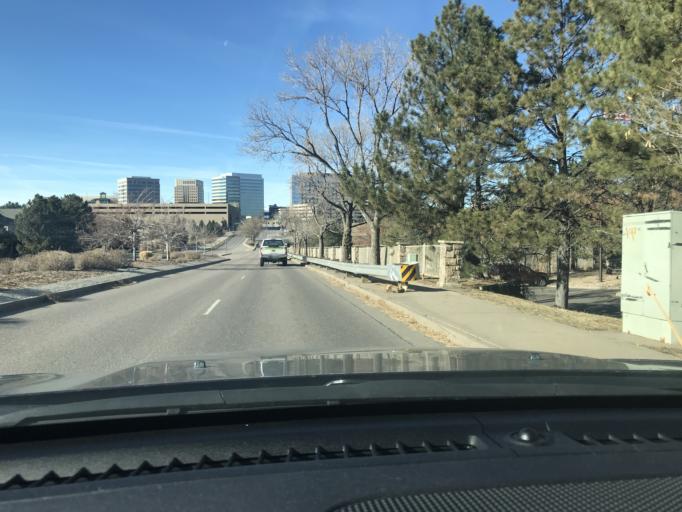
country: US
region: Colorado
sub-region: Arapahoe County
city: Centennial
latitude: 39.6025
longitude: -104.8814
